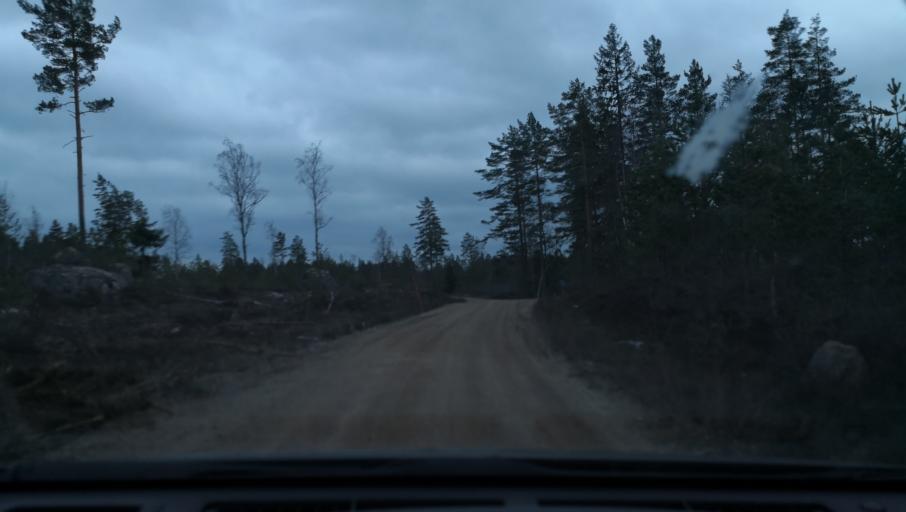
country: SE
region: OErebro
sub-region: Lindesbergs Kommun
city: Fellingsbro
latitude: 59.6059
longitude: 15.5773
